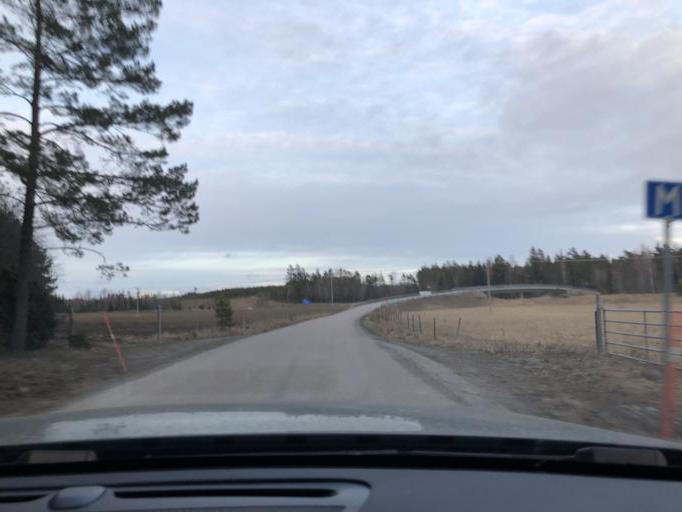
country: SE
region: Uppsala
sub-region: Uppsala Kommun
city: Gamla Uppsala
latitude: 59.9228
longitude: 17.6521
